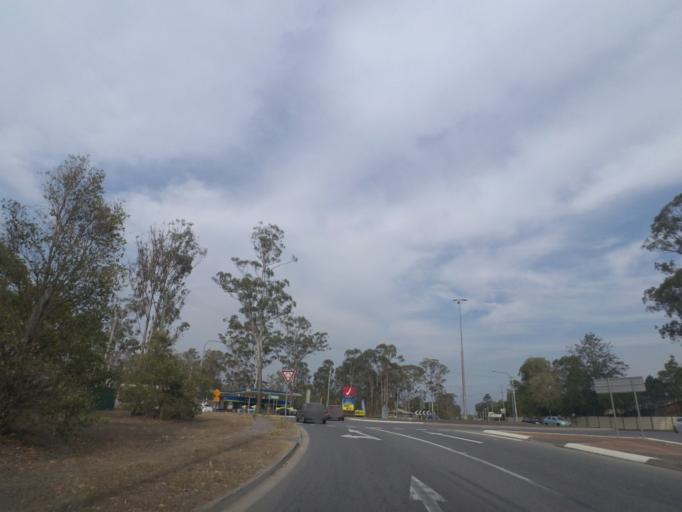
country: AU
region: Queensland
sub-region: Brisbane
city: Sunnybank
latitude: -27.5961
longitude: 153.0177
